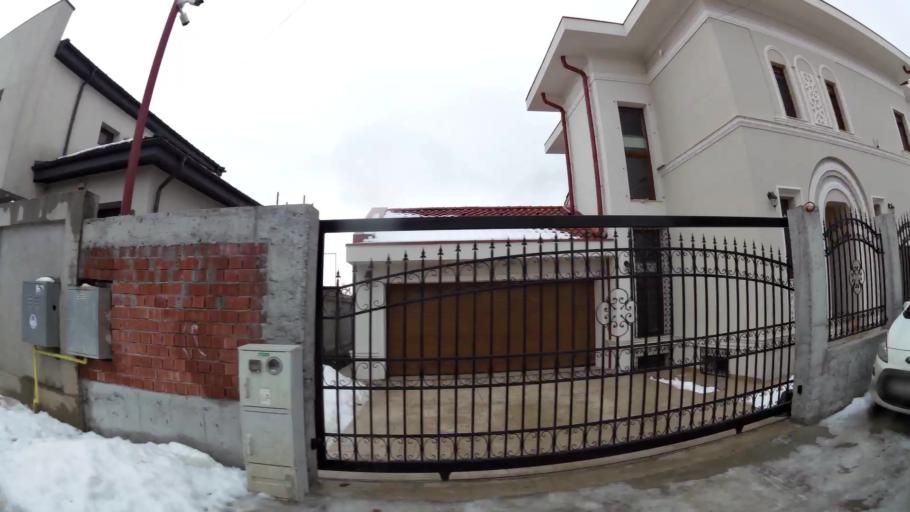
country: RO
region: Ilfov
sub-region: Comuna Pantelimon
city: Pantelimon
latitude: 44.4560
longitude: 26.2195
